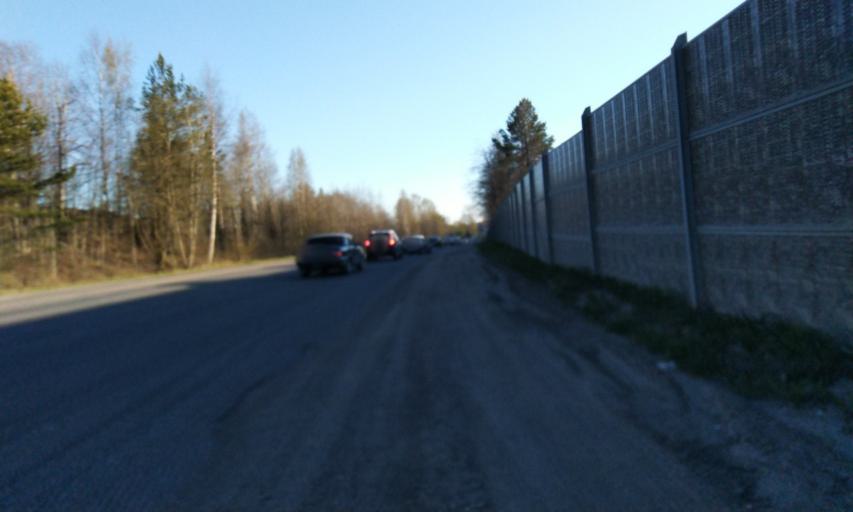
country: RU
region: Leningrad
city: Toksovo
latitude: 60.1245
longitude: 30.5138
